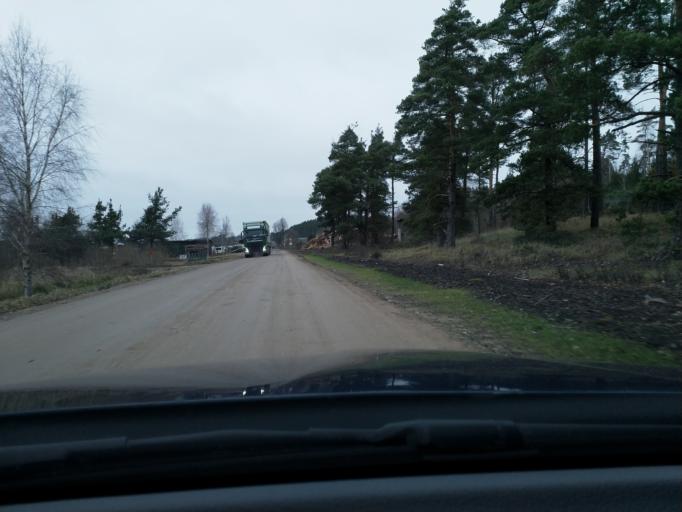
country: LV
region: Ventspils Rajons
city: Piltene
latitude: 57.1283
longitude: 21.8017
